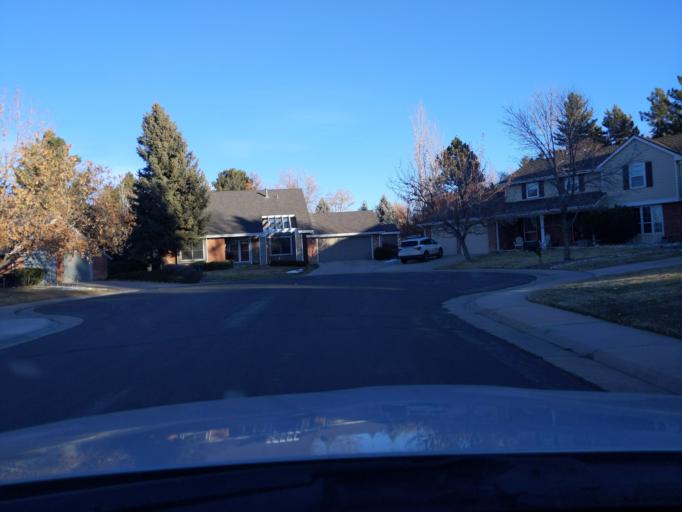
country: US
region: Colorado
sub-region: Douglas County
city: Acres Green
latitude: 39.5700
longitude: -104.8903
